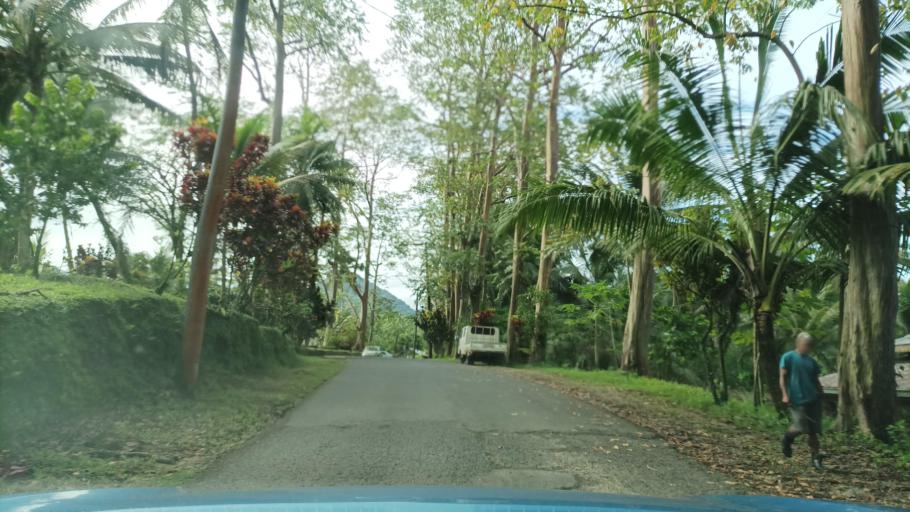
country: FM
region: Pohnpei
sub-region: Kolonia Municipality
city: Kolonia
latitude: 6.9418
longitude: 158.2248
